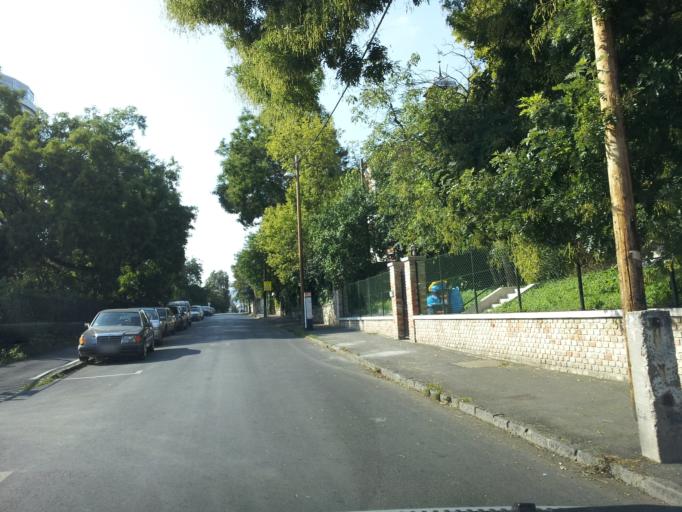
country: HU
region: Budapest
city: Budapest II. keruelet
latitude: 47.5101
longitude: 19.0149
